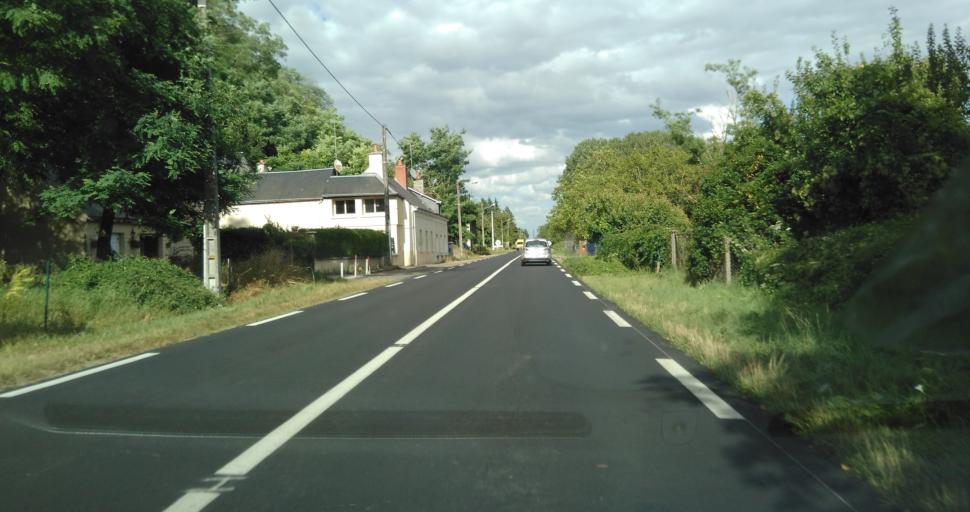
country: FR
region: Centre
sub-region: Departement d'Indre-et-Loire
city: Langeais
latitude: 47.3140
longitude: 0.3767
